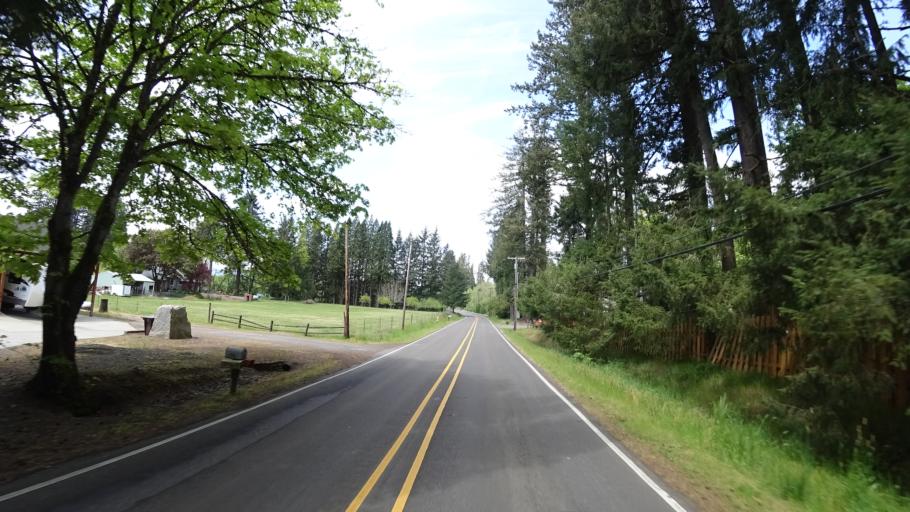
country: US
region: Oregon
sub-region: Washington County
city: Hillsboro
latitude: 45.5417
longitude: -123.0014
